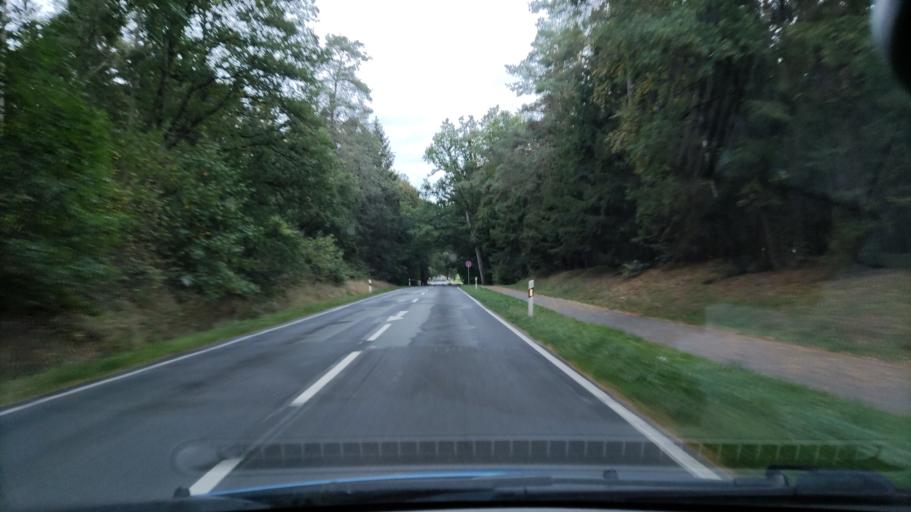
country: DE
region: Mecklenburg-Vorpommern
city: Lubtheen
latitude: 53.3839
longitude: 10.9671
